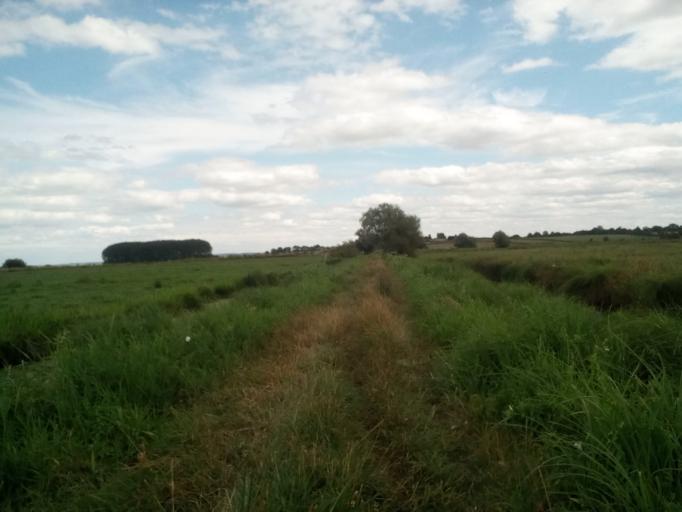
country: FR
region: Lower Normandy
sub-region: Departement du Calvados
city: Troarn
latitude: 49.1741
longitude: -0.1571
